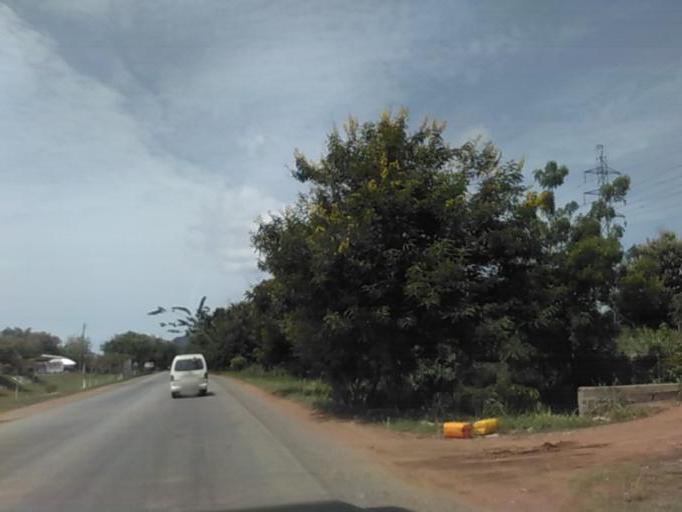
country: GH
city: Akropong
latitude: 6.1213
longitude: 0.0481
